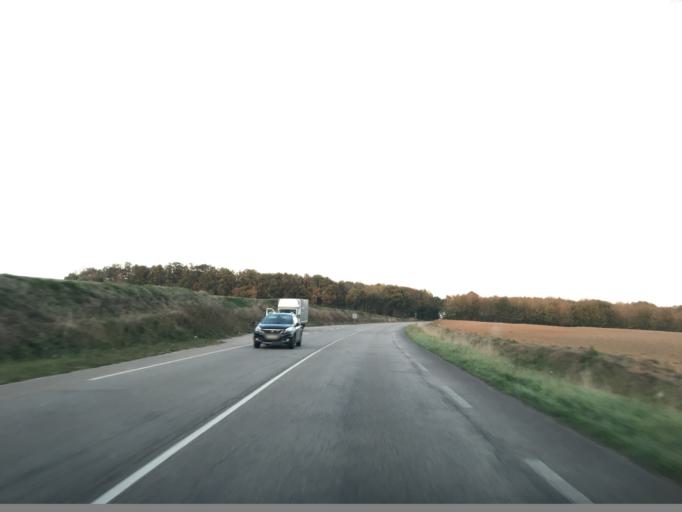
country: FR
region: Haute-Normandie
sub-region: Departement de l'Eure
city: Bourth
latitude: 48.6999
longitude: 0.8306
